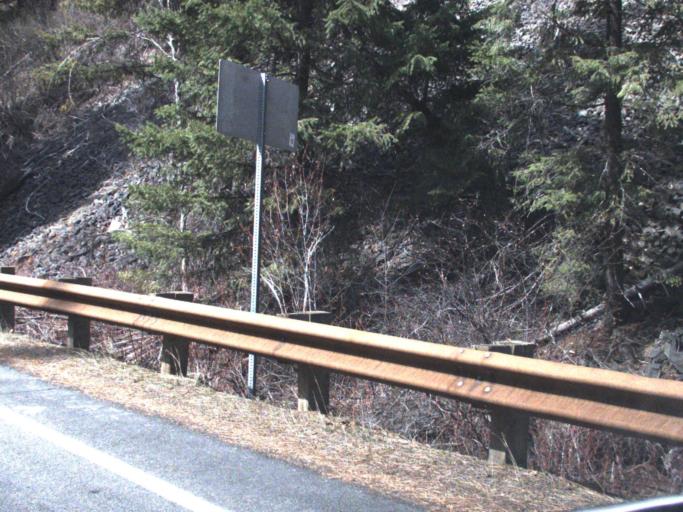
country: US
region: Washington
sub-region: Kittitas County
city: Cle Elum
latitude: 46.9870
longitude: -121.1147
